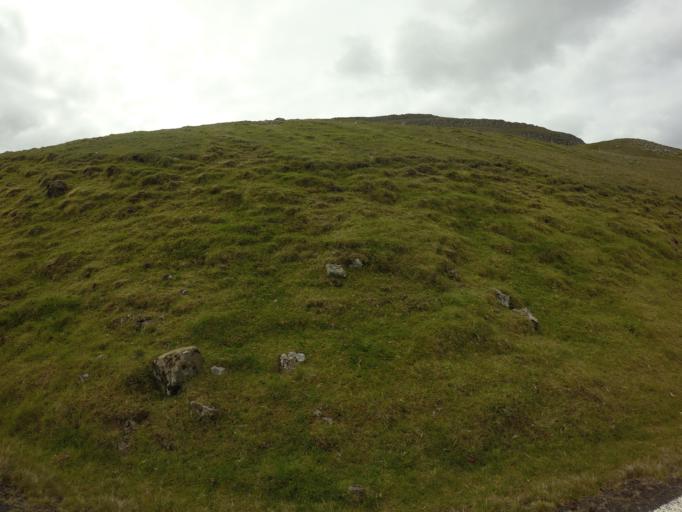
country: FO
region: Suduroy
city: Tvoroyri
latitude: 61.5242
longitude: -6.8254
